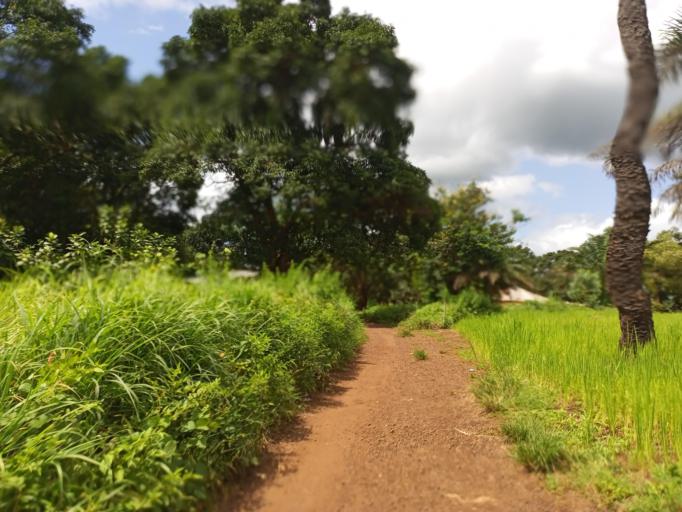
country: SL
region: Northern Province
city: Kamakwie
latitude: 9.4989
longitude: -12.2365
